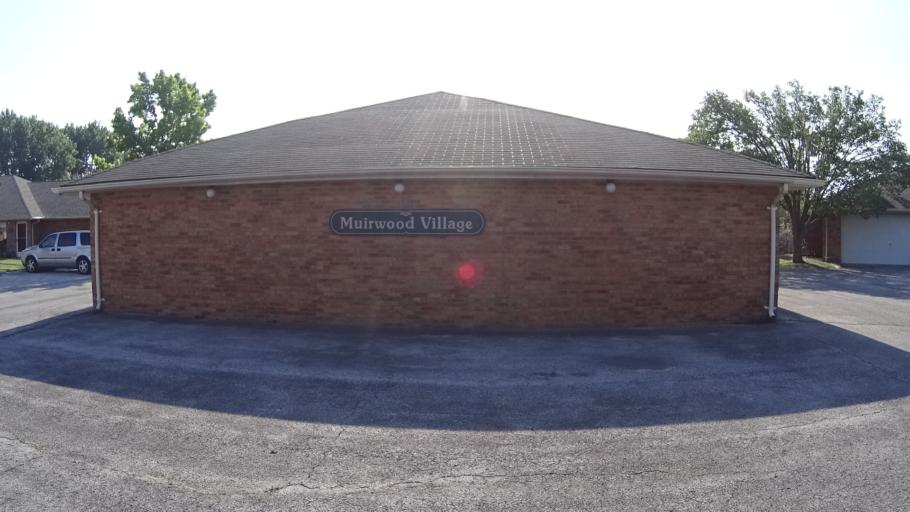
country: US
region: Ohio
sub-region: Erie County
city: Sandusky
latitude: 41.4471
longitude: -82.7859
